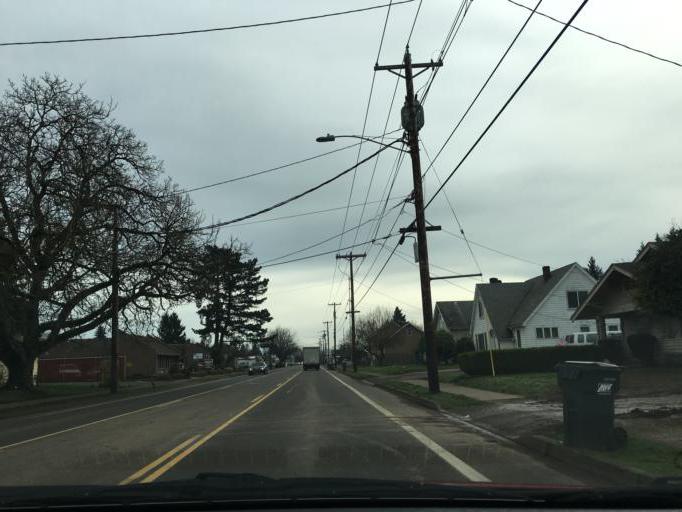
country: US
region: Oregon
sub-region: Marion County
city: Woodburn
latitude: 45.1387
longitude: -122.8482
